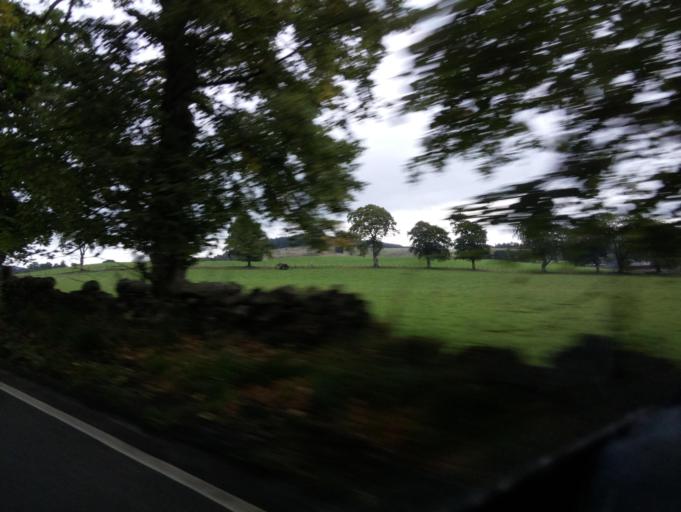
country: GB
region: Scotland
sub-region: Clackmannanshire
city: Dollar
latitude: 56.1738
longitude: -3.6357
